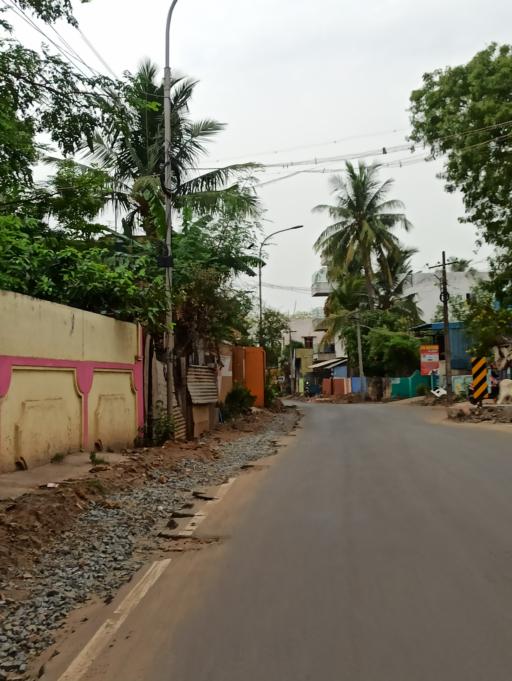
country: IN
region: Tamil Nadu
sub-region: Thiruvallur
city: Chinnasekkadu
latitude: 13.1678
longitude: 80.2397
